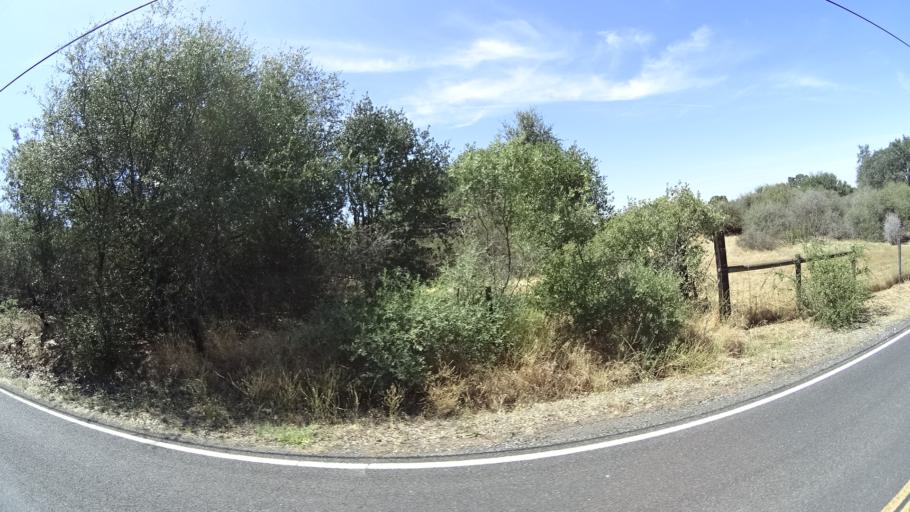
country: US
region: California
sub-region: Calaveras County
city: Rancho Calaveras
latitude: 38.1484
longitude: -120.9425
